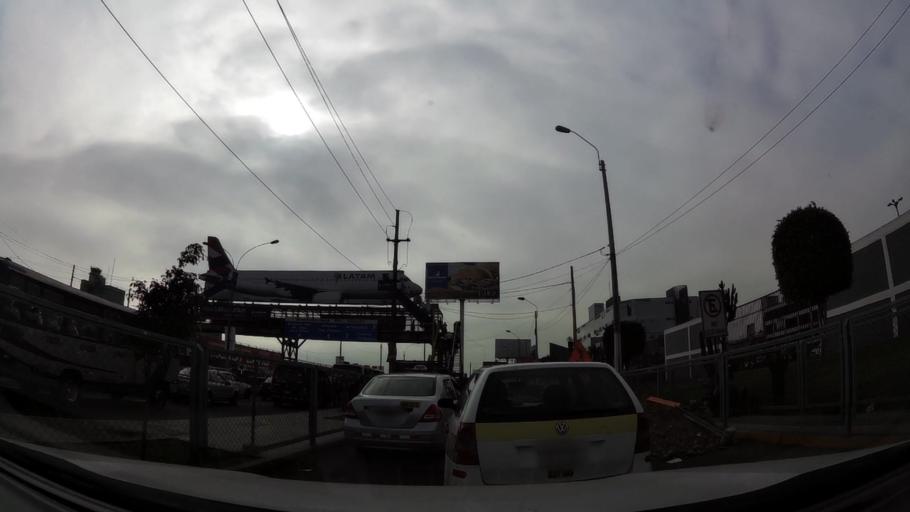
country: PE
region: Callao
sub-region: Callao
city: Callao
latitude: -12.0240
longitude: -77.1049
